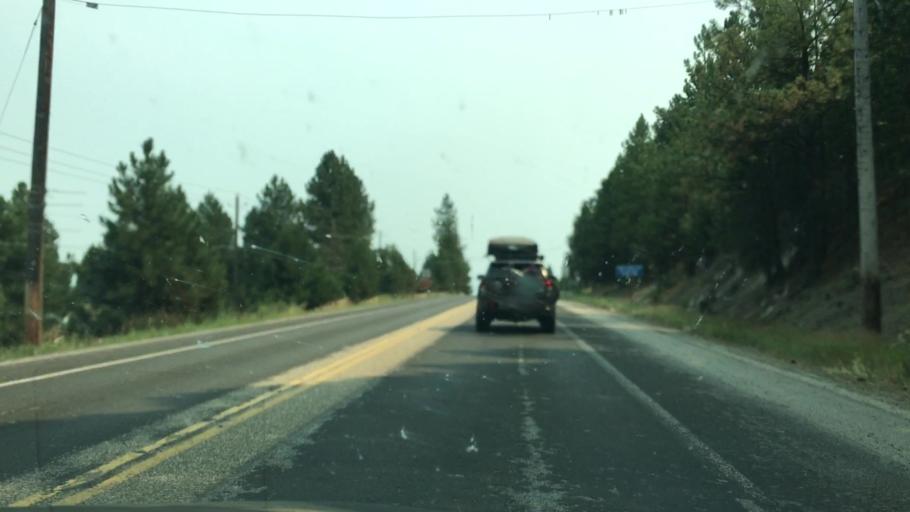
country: US
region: Idaho
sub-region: Valley County
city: Cascade
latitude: 44.5106
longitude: -116.0364
